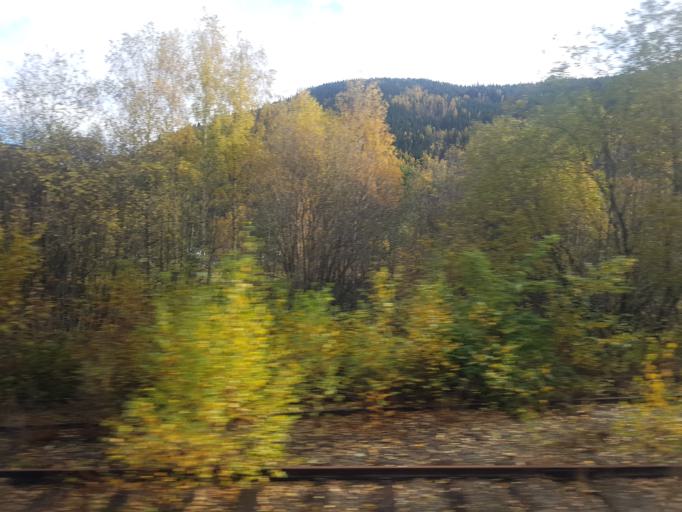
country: NO
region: Oppland
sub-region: Sel
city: Otta
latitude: 61.8009
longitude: 9.5520
